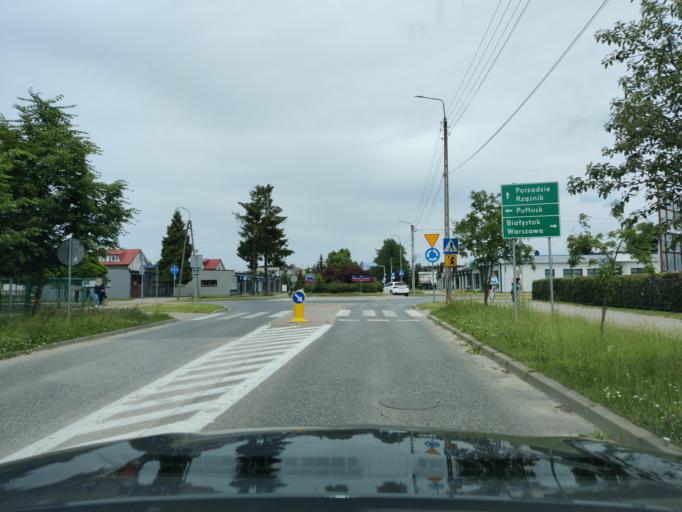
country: PL
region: Masovian Voivodeship
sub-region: Powiat wyszkowski
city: Wyszkow
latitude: 52.6029
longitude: 21.4553
